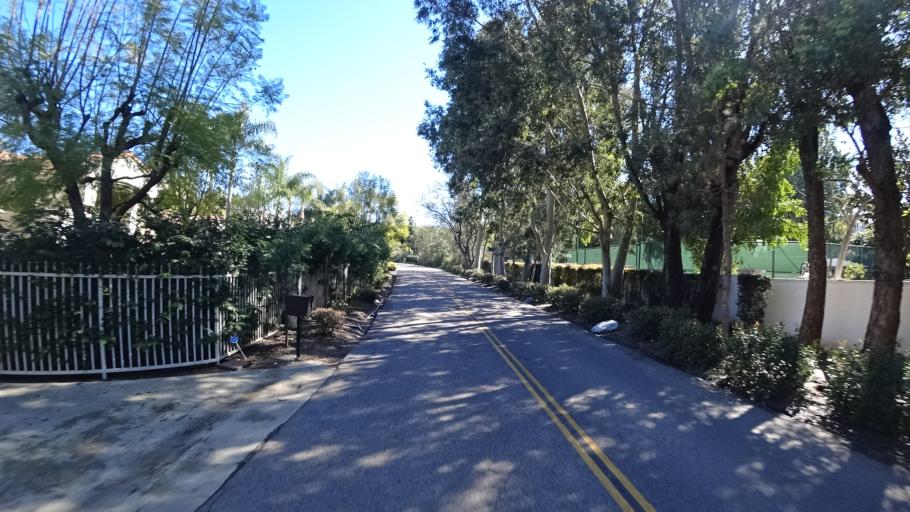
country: US
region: California
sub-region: Orange County
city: Villa Park
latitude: 33.8481
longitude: -117.8121
